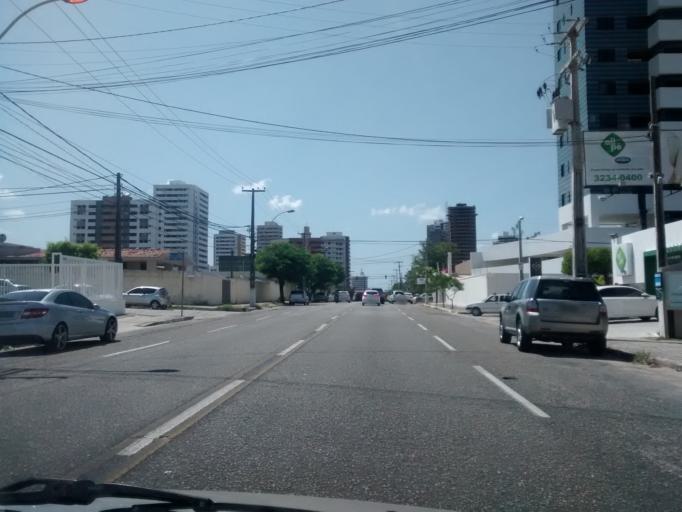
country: BR
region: Rio Grande do Norte
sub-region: Natal
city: Natal
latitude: -5.8201
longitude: -35.2176
